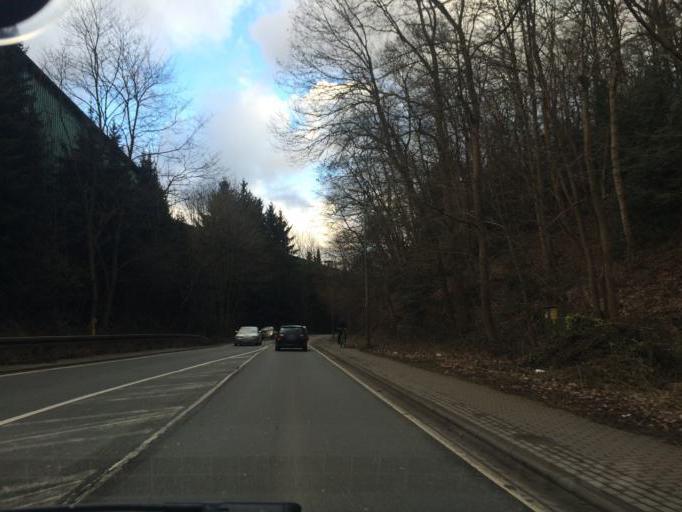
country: DE
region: North Rhine-Westphalia
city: Sprockhovel
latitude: 51.4061
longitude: 7.2524
